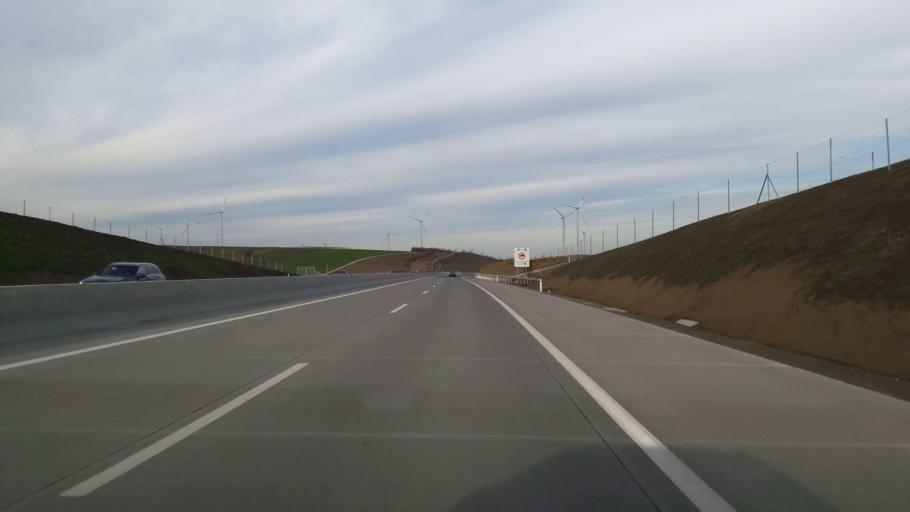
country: AT
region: Lower Austria
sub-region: Politischer Bezirk Mistelbach
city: Wilfersdorf
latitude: 48.5889
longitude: 16.6287
